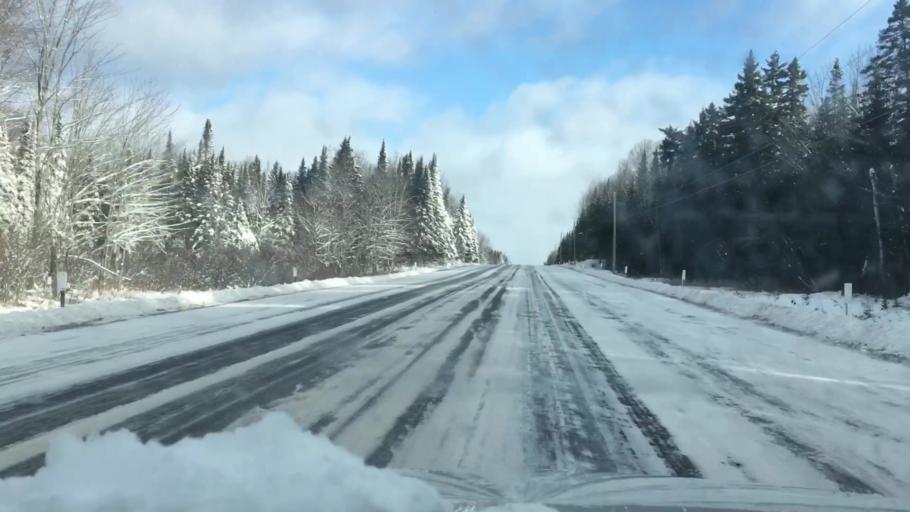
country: US
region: Maine
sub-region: Aroostook County
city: Van Buren
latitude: 47.0490
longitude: -67.9980
